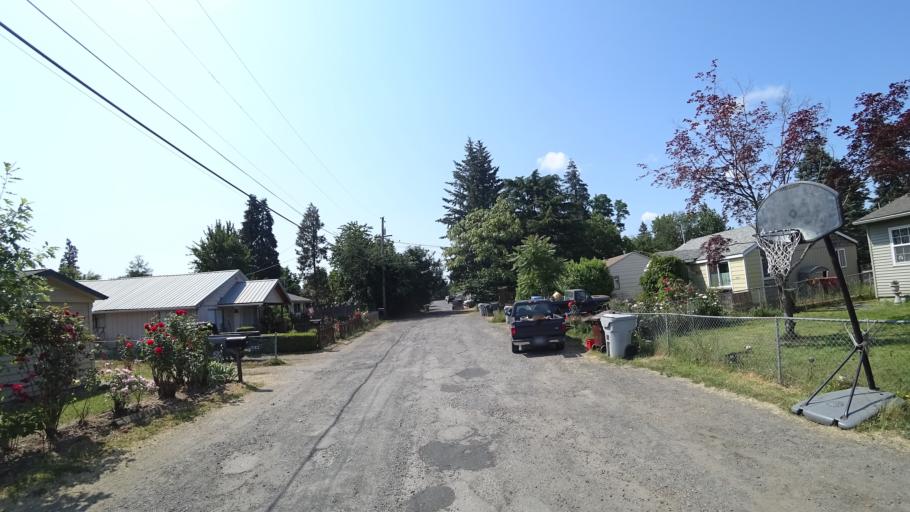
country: US
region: Oregon
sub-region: Multnomah County
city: Lents
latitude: 45.4539
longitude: -122.5865
